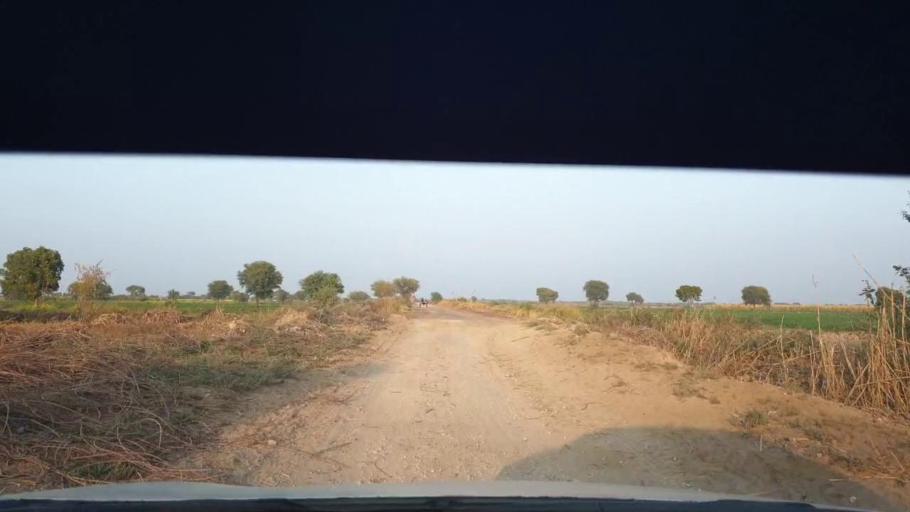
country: PK
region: Sindh
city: Berani
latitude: 25.7420
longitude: 68.9692
